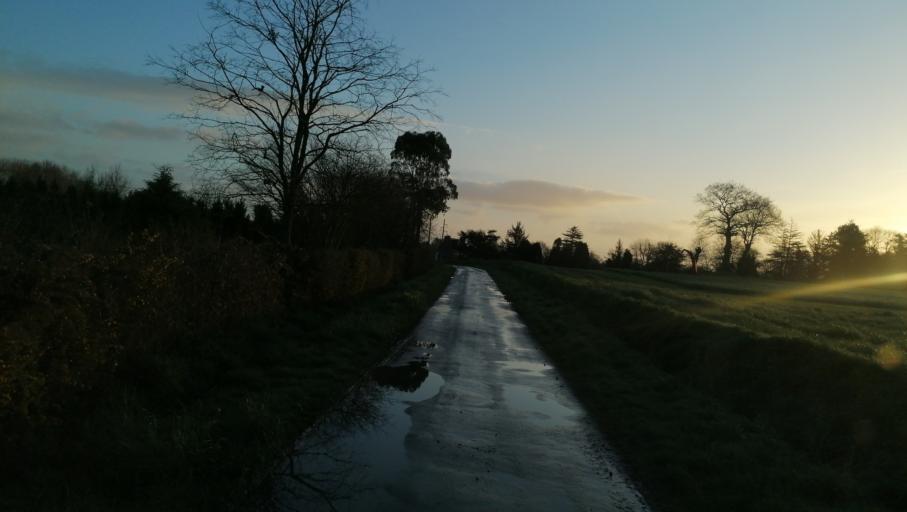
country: FR
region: Brittany
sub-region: Departement des Cotes-d'Armor
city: Plouha
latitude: 48.6608
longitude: -2.9359
